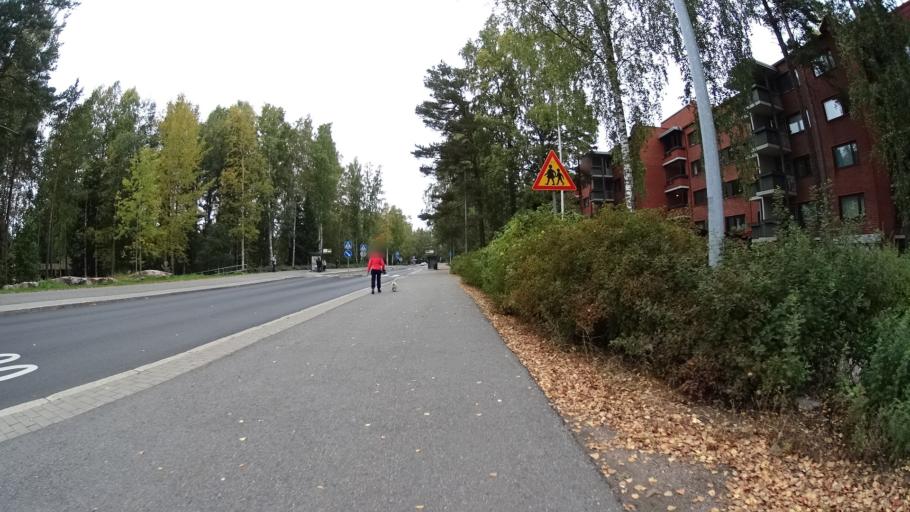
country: FI
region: Uusimaa
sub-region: Helsinki
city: Vantaa
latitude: 60.2214
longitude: 25.0580
